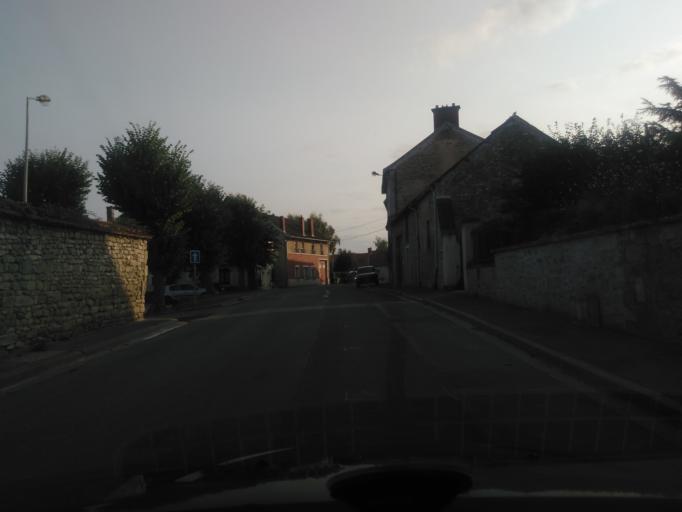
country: FR
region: Champagne-Ardenne
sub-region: Departement de la Marne
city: Fismes
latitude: 49.2691
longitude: 3.6974
